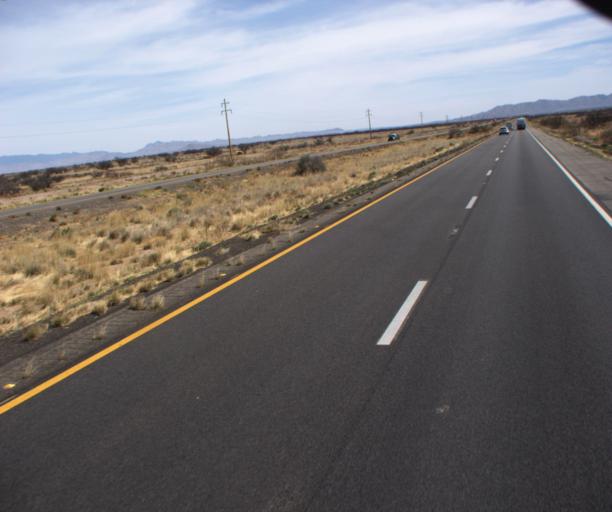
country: US
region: Arizona
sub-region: Cochise County
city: Willcox
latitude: 32.1892
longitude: -109.9277
